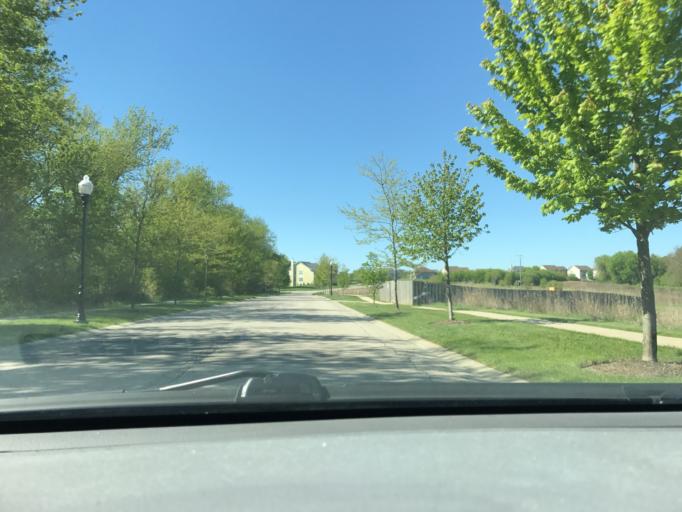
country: US
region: Illinois
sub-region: Kane County
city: Pingree Grove
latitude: 42.0472
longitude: -88.3640
